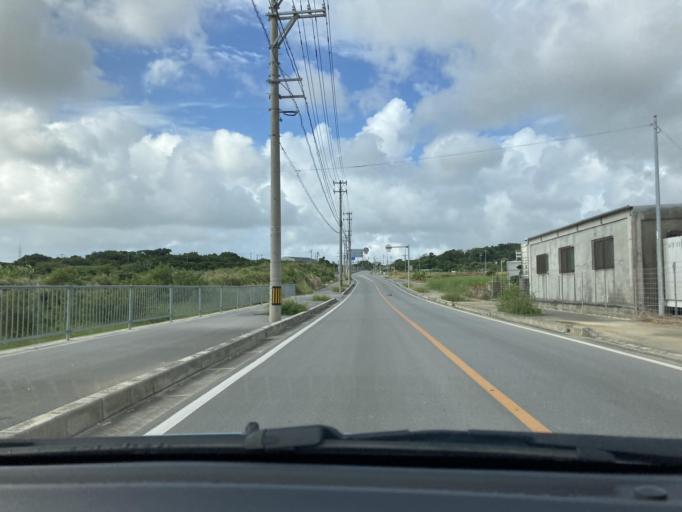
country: JP
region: Okinawa
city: Itoman
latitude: 26.1155
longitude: 127.6920
